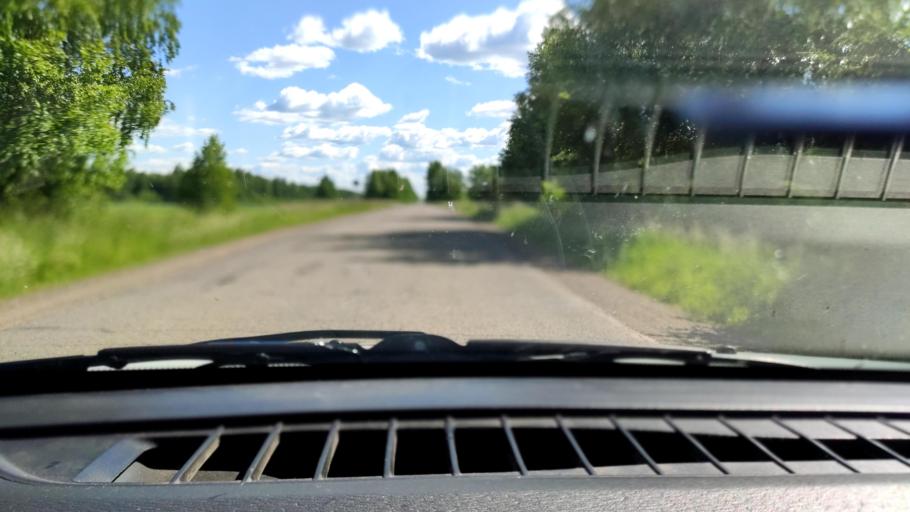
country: RU
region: Perm
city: Kukushtan
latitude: 57.2877
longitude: 56.5361
